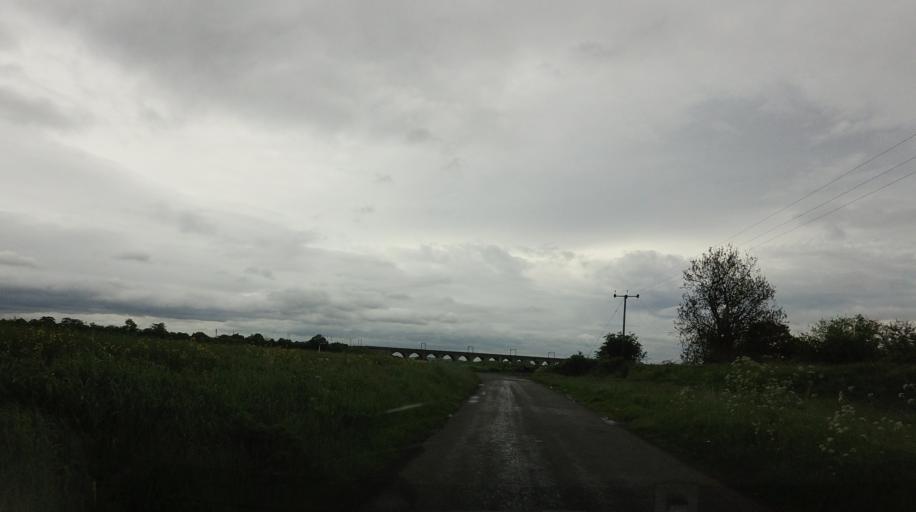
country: GB
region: Scotland
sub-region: Edinburgh
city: Newbridge
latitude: 55.9322
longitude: -3.4321
